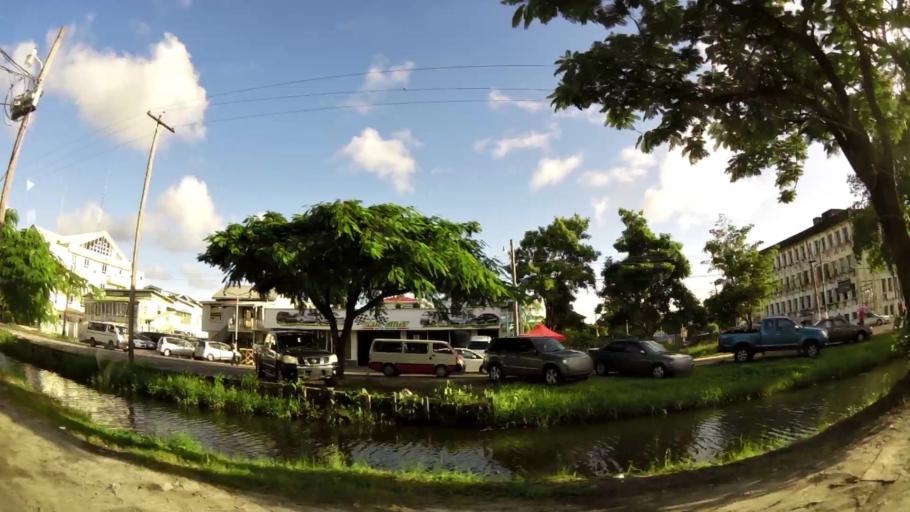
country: GY
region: Demerara-Mahaica
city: Georgetown
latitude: 6.8095
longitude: -58.1640
